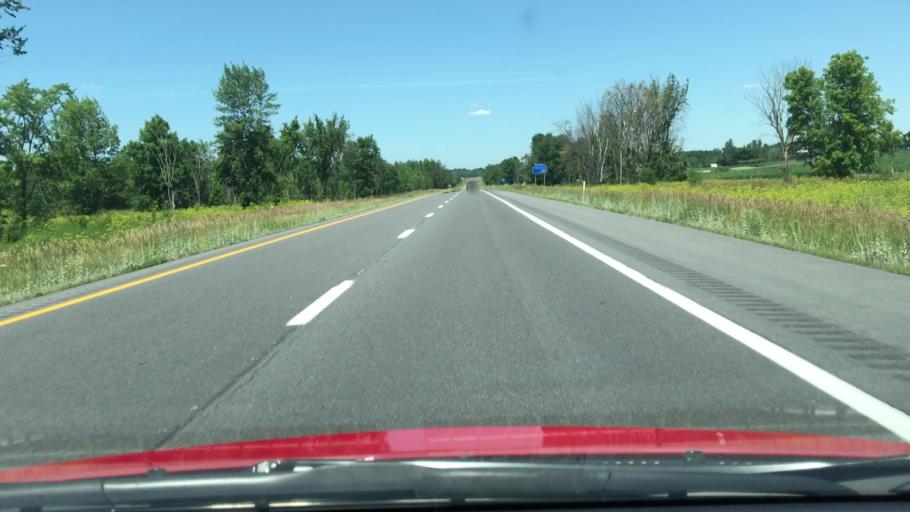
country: US
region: New York
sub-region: Clinton County
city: Cumberland Head
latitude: 44.7697
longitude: -73.4333
